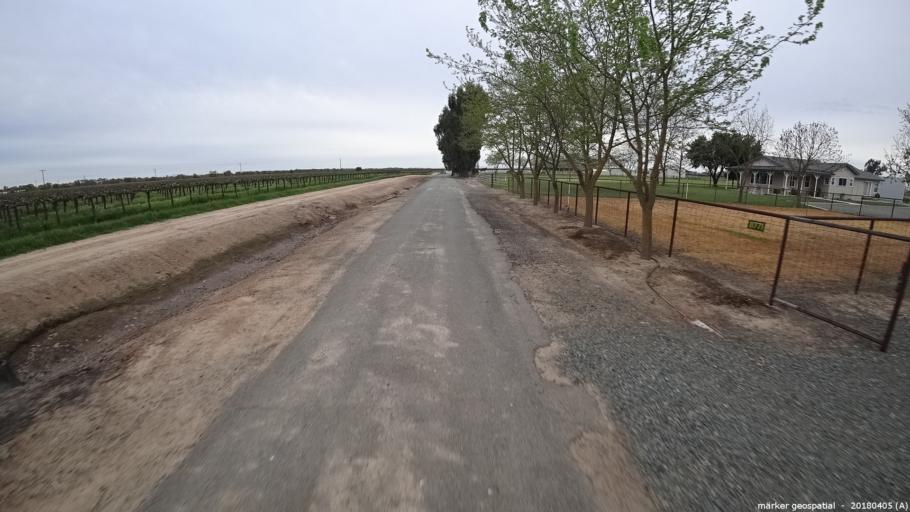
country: US
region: California
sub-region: Sacramento County
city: Herald
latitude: 38.3176
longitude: -121.2408
